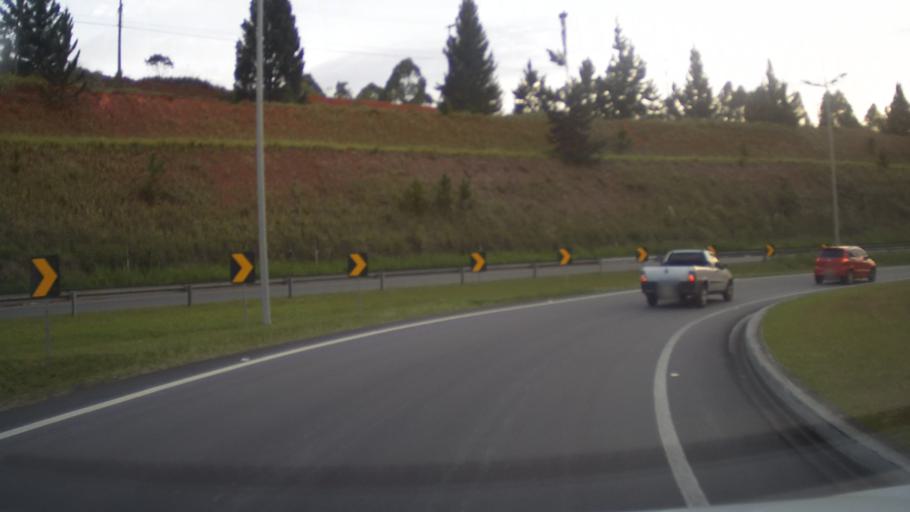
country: BR
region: Sao Paulo
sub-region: Aruja
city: Aruja
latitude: -23.4036
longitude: -46.3284
